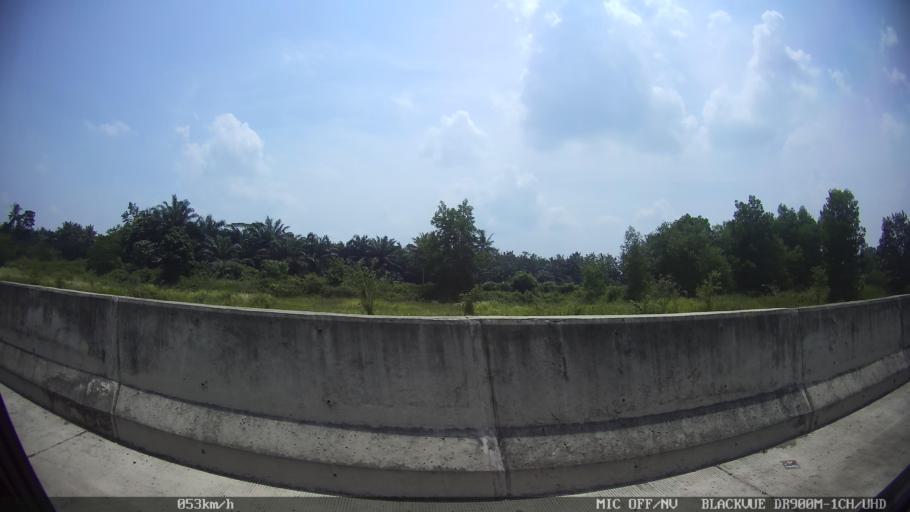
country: ID
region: Lampung
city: Natar
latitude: -5.3140
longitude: 105.2572
